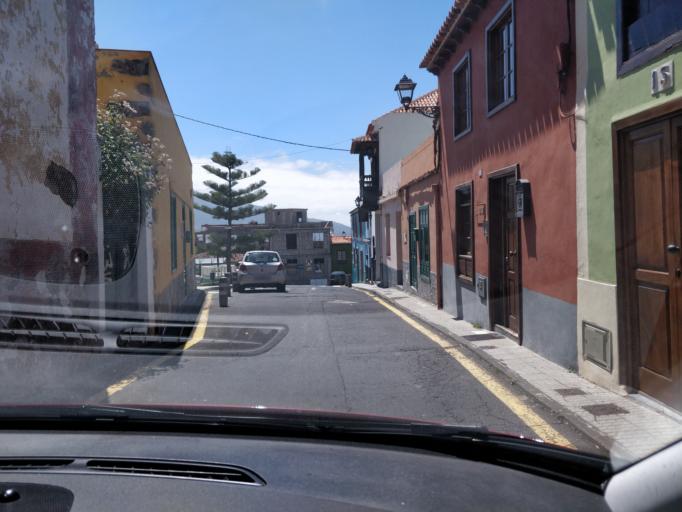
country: ES
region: Canary Islands
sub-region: Provincia de Santa Cruz de Tenerife
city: La Orotava
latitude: 28.3847
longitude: -16.5211
